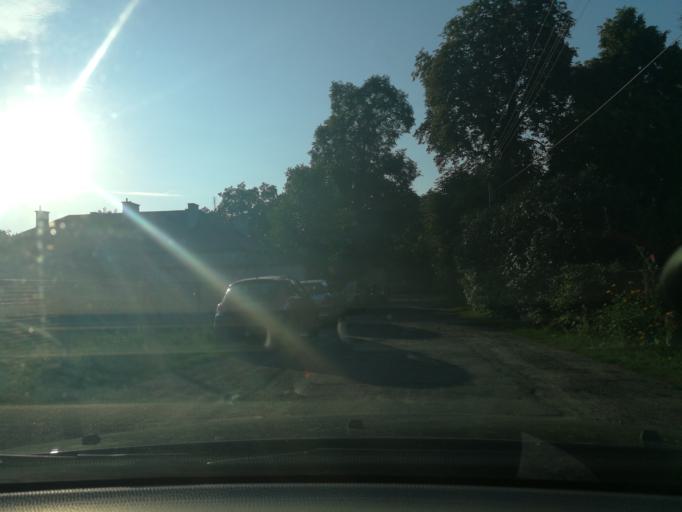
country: PL
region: Masovian Voivodeship
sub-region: Powiat pruszkowski
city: Brwinow
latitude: 52.1366
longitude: 20.7116
